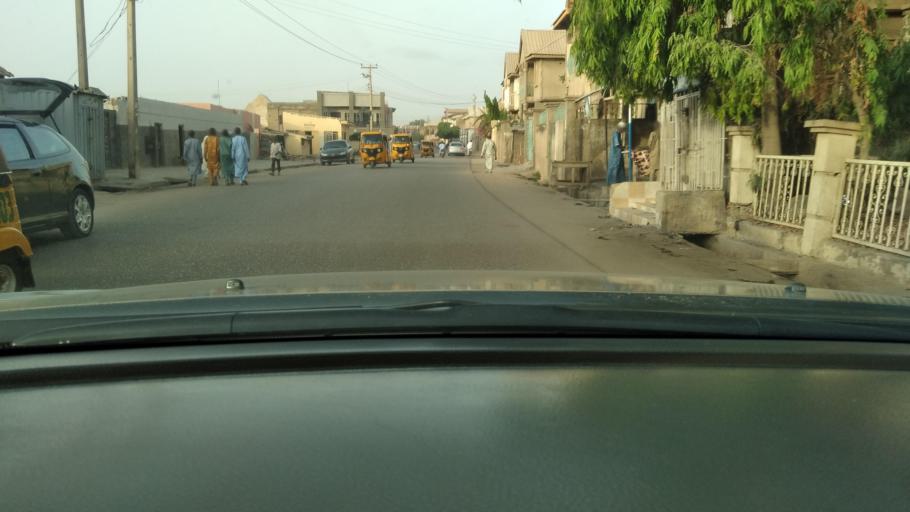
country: NG
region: Kano
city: Kano
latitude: 11.9586
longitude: 8.5234
